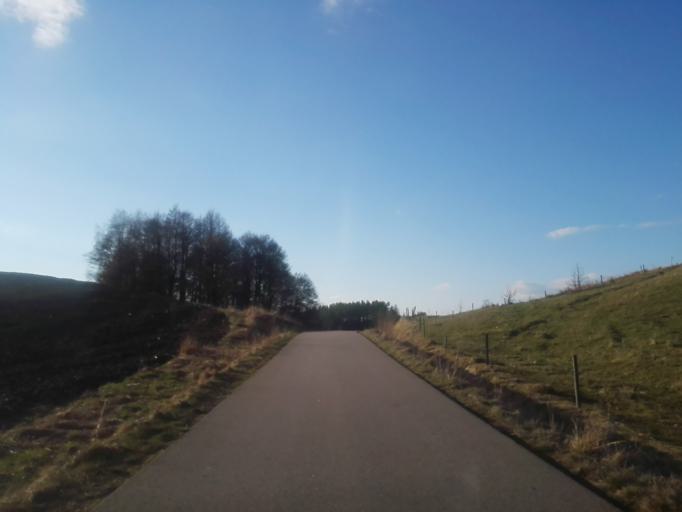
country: PL
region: Podlasie
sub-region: Suwalki
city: Suwalki
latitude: 54.2121
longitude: 23.0046
